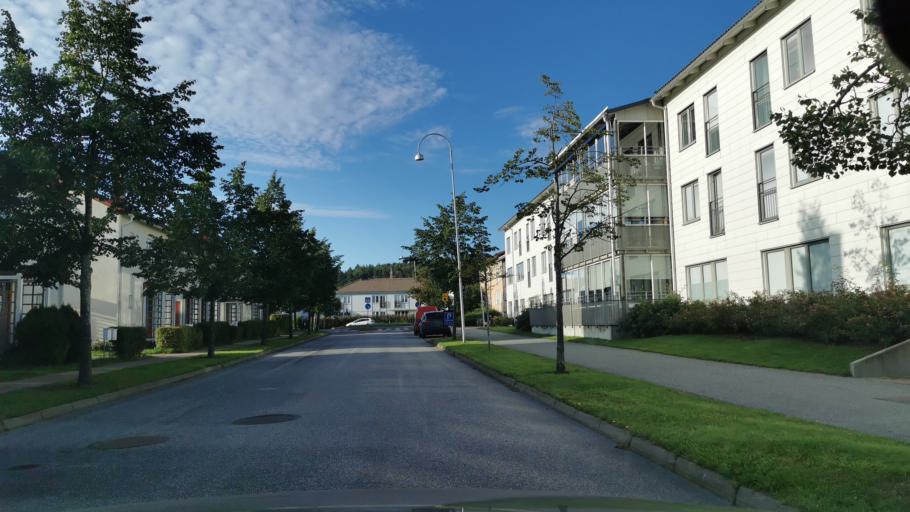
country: SE
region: Vaestra Goetaland
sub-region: Molndal
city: Moelndal
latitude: 57.6527
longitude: 11.9642
